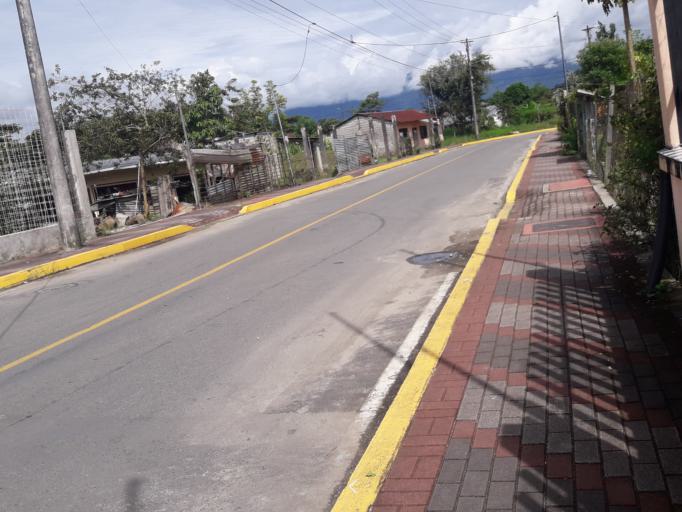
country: EC
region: Napo
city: Tena
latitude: -1.0059
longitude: -77.8175
